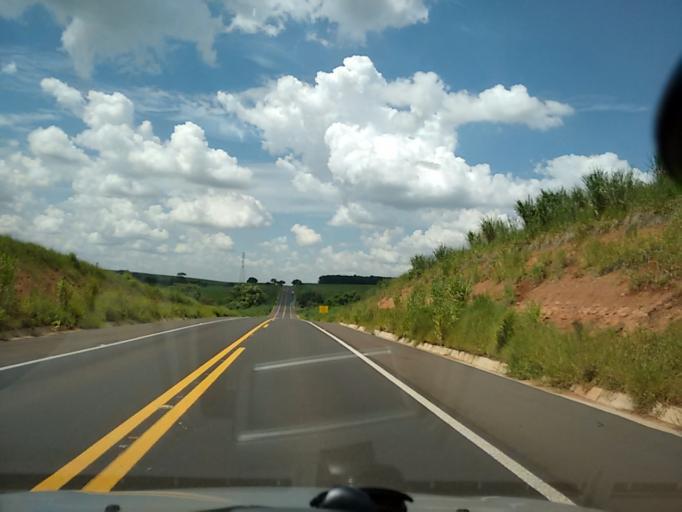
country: BR
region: Sao Paulo
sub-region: Osvaldo Cruz
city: Osvaldo Cruz
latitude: -21.8714
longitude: -50.8557
